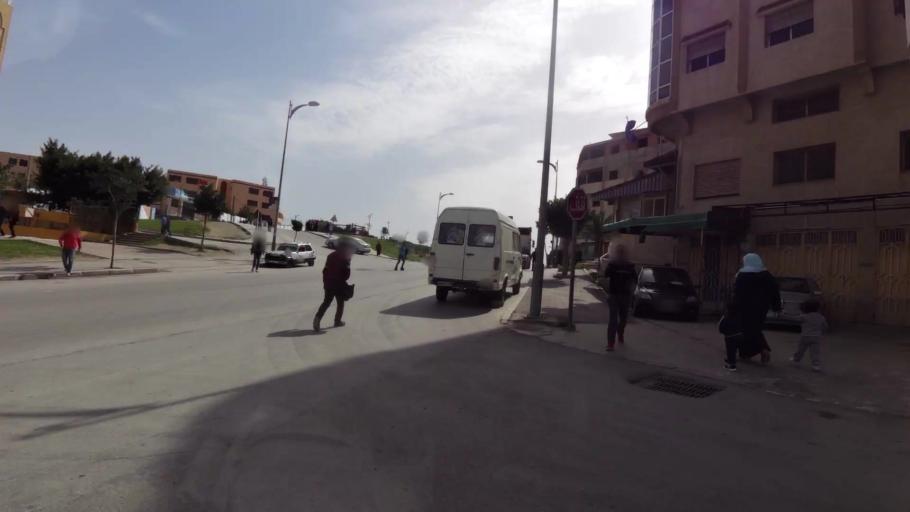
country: MA
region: Tanger-Tetouan
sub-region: Tanger-Assilah
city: Tangier
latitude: 35.7379
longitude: -5.8328
